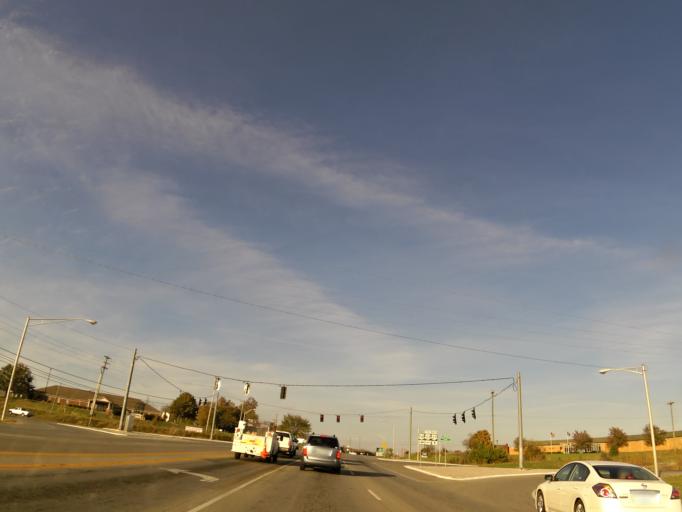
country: US
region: Kentucky
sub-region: Lincoln County
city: Stanford
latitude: 37.5401
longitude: -84.6525
